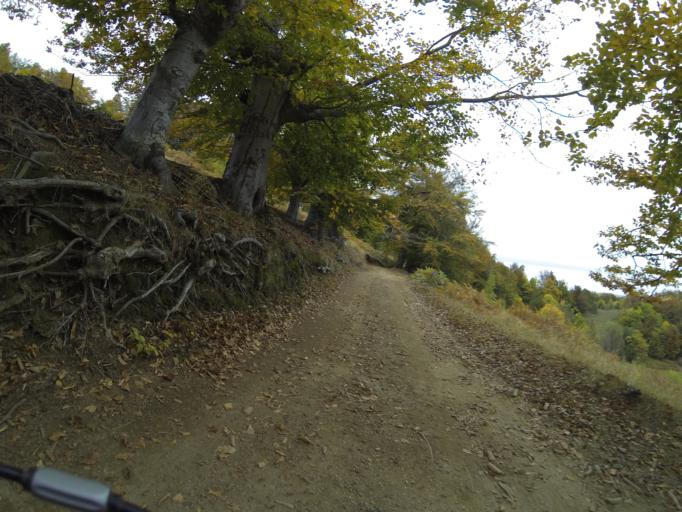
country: RO
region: Gorj
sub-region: Comuna Pades
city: Closani
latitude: 45.0920
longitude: 22.8380
